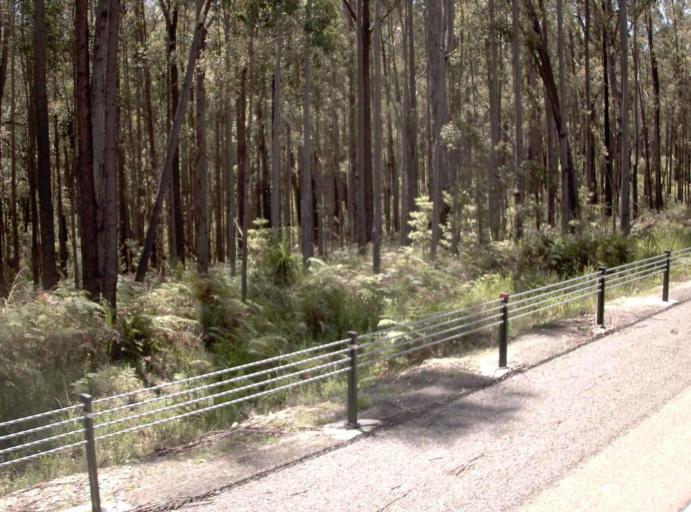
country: AU
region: Victoria
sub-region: East Gippsland
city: Lakes Entrance
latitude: -37.6624
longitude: 148.8007
